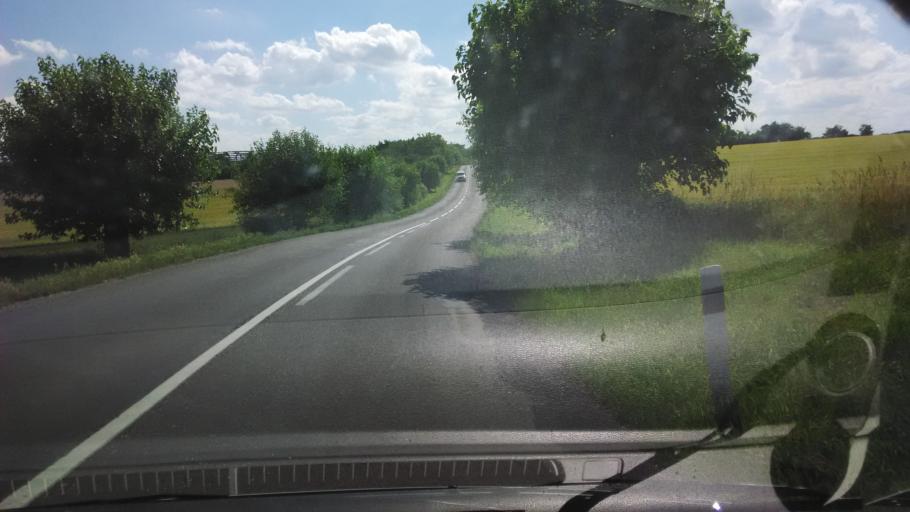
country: SK
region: Nitriansky
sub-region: Okres Nitra
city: Vrable
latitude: 48.1513
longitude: 18.4240
